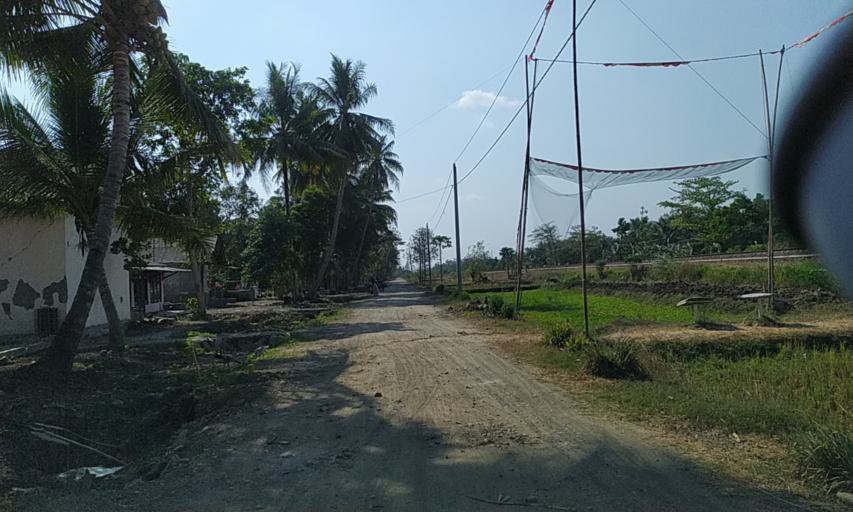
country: ID
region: Central Java
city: Alurbulu
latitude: -7.5049
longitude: 108.8336
